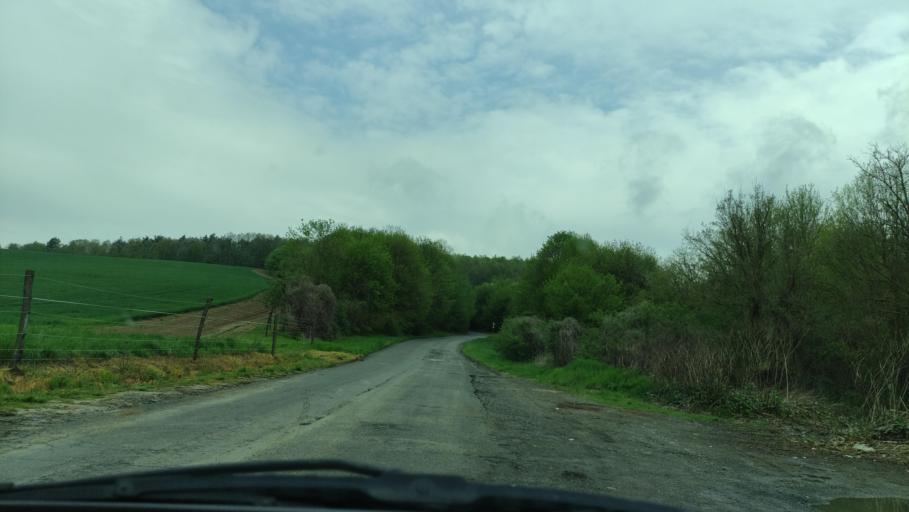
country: HU
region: Baranya
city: Komlo
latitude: 46.2252
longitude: 18.2360
